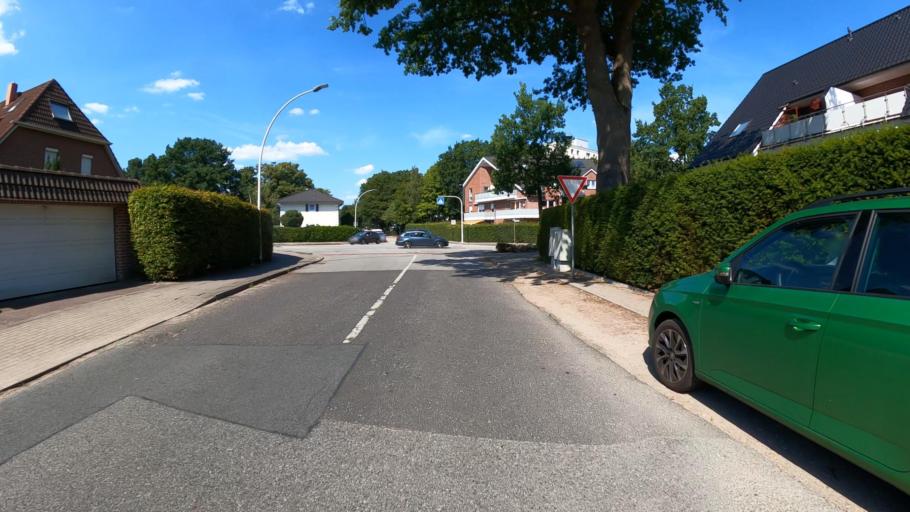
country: DE
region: Schleswig-Holstein
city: Halstenbek
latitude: 53.6179
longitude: 9.8706
